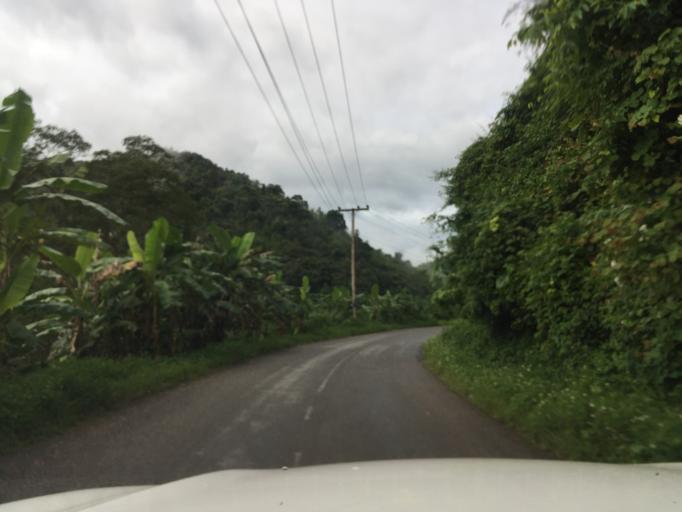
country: LA
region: Phongsali
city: Khoa
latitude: 21.0929
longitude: 102.2467
